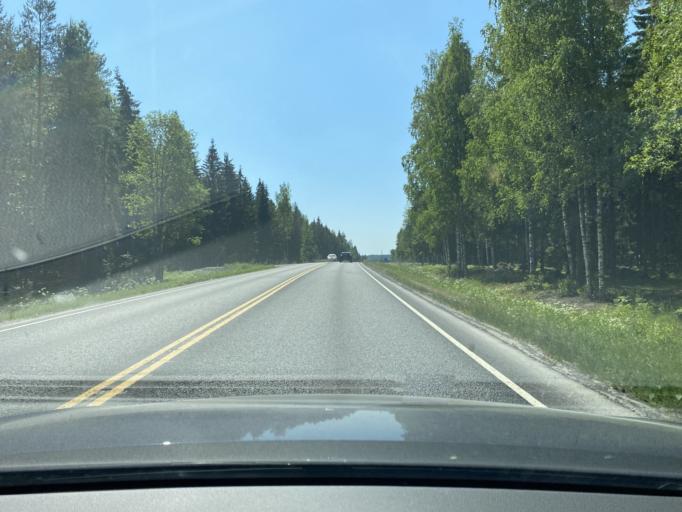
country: FI
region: Pirkanmaa
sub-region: Tampere
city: Nokia
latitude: 61.4099
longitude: 23.3003
